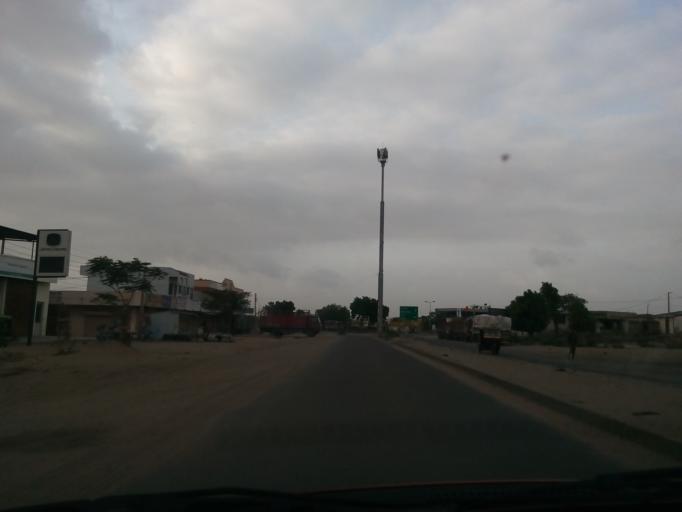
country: IN
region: Gujarat
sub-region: Kachchh
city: Bhuj
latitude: 23.2482
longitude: 69.6998
